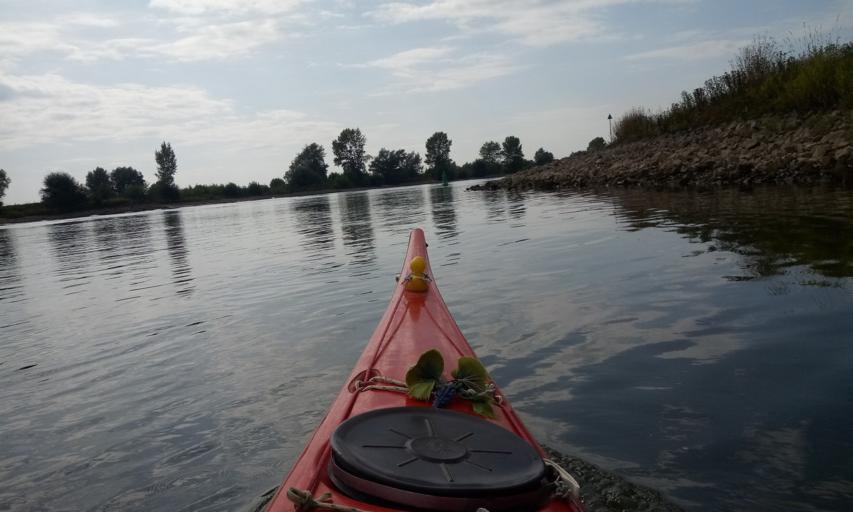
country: NL
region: Gelderland
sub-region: Gemeente Lochem
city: Gorssel
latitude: 52.2020
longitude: 6.1734
